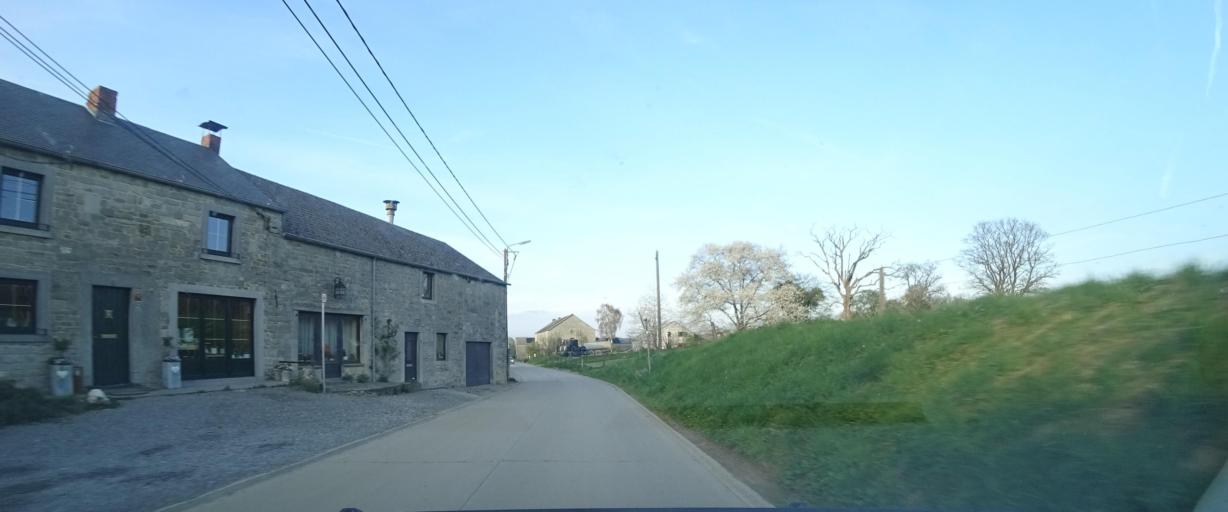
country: BE
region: Wallonia
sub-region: Province de Namur
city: Hamois
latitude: 50.3150
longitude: 5.1499
